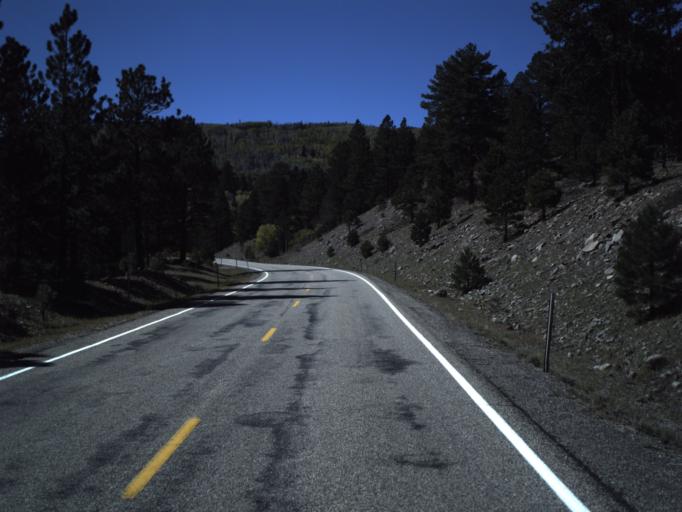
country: US
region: Utah
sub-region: Wayne County
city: Loa
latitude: 38.0962
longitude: -111.3430
